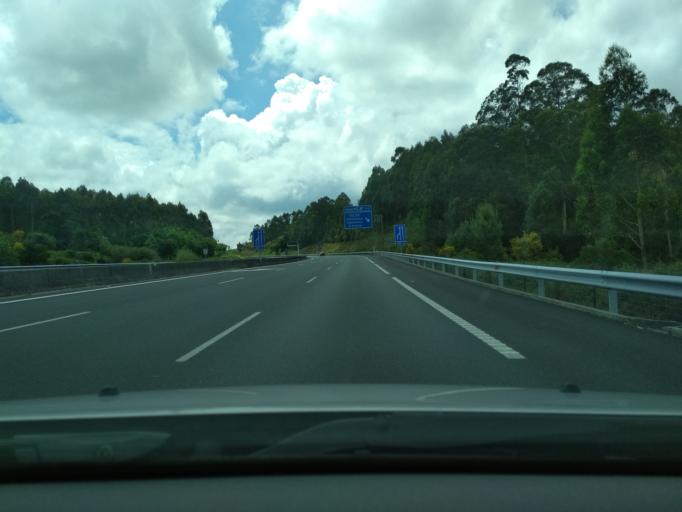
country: ES
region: Galicia
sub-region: Provincia de Pontevedra
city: Barro
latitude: 42.5304
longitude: -8.6701
